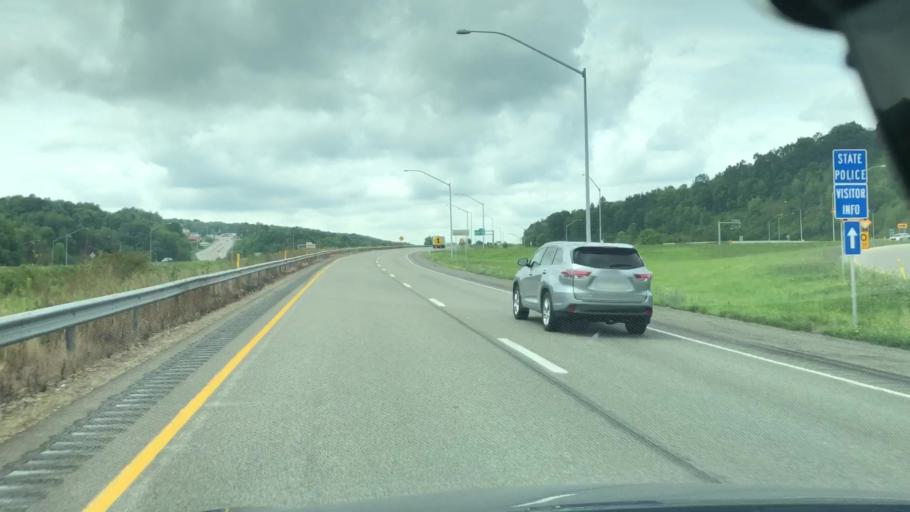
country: US
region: Pennsylvania
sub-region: Crawford County
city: Meadville
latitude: 41.6201
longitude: -80.1769
